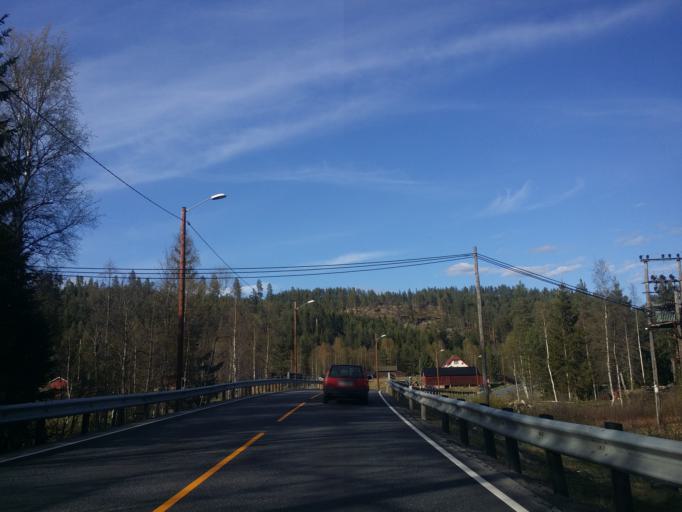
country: NO
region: Buskerud
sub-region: Kongsberg
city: Kongsberg
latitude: 59.6262
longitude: 9.4747
